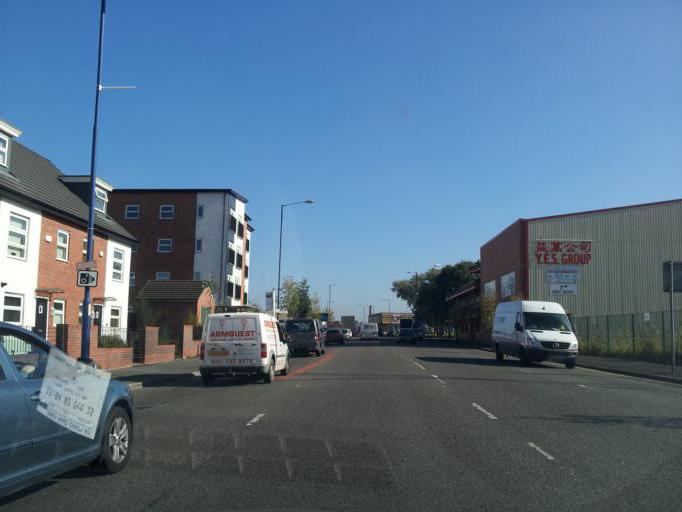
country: GB
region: England
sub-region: Manchester
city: Failsworth
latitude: 53.5028
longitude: -2.1828
